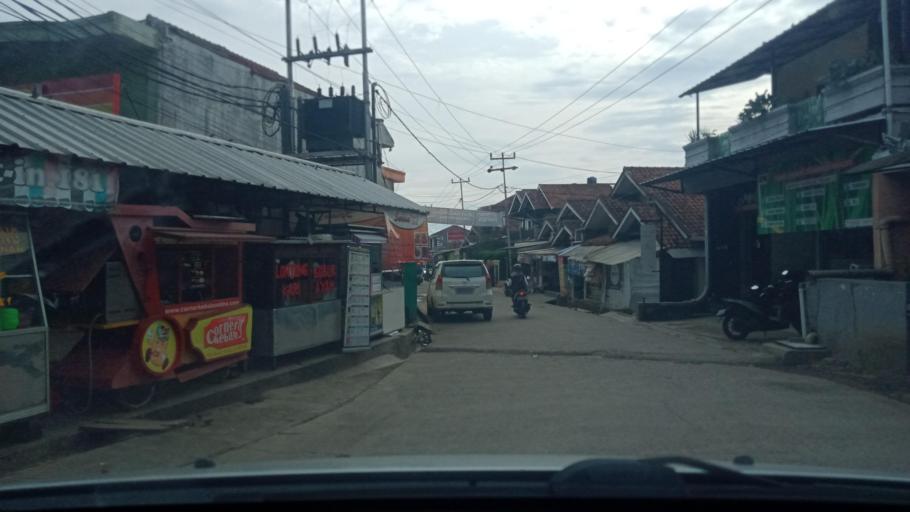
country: ID
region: West Java
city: Lembang
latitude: -6.8040
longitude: 107.5882
